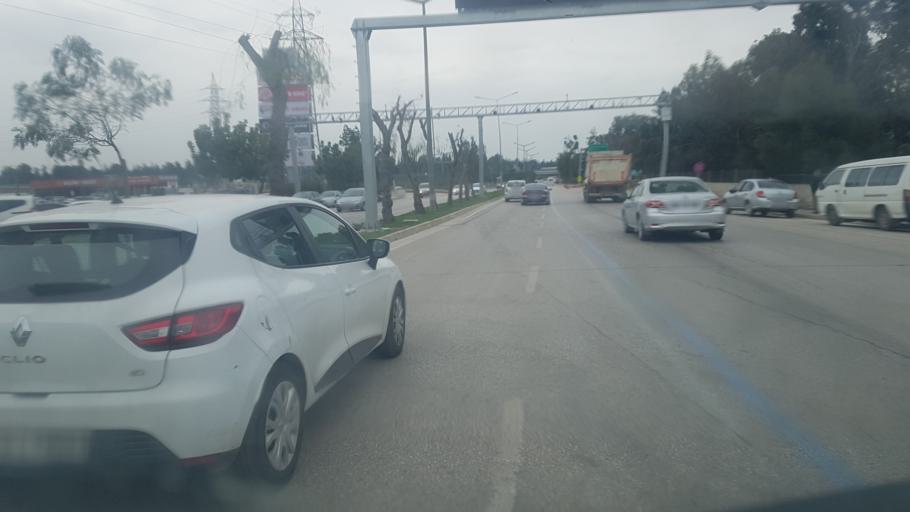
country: TR
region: Adana
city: Adana
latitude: 37.0279
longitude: 35.3448
